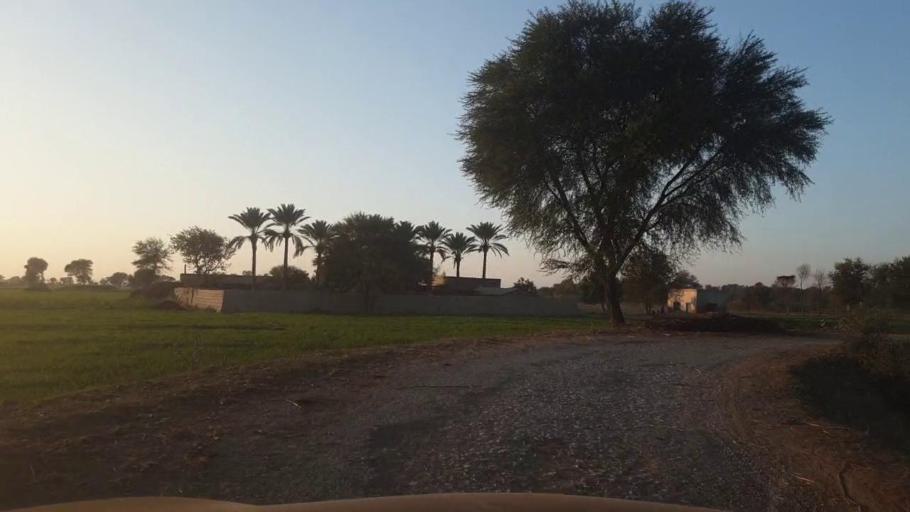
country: PK
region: Sindh
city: Ubauro
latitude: 28.1821
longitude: 69.6026
